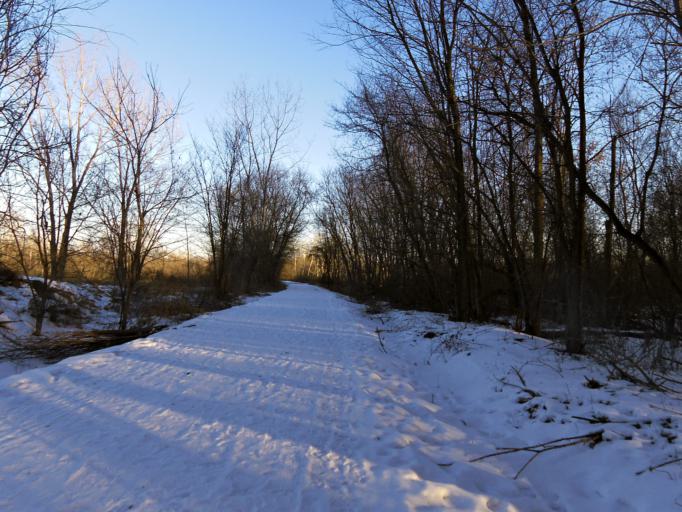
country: US
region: Minnesota
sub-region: Washington County
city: Stillwater
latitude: 45.0705
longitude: -92.8491
